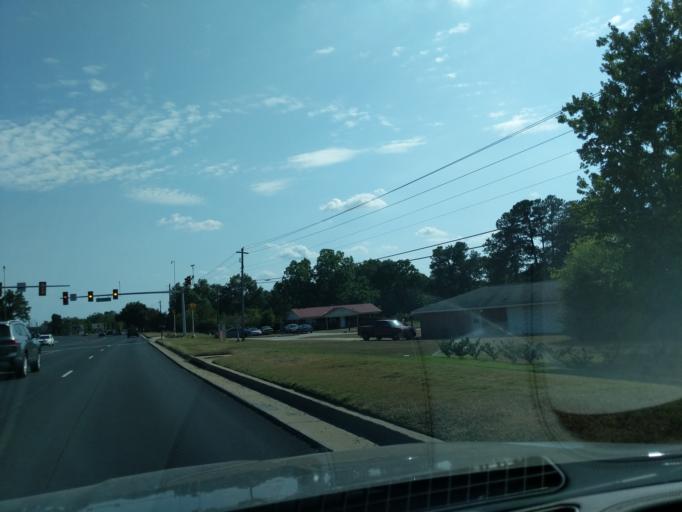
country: US
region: Georgia
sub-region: Columbia County
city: Evans
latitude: 33.4937
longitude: -82.1374
